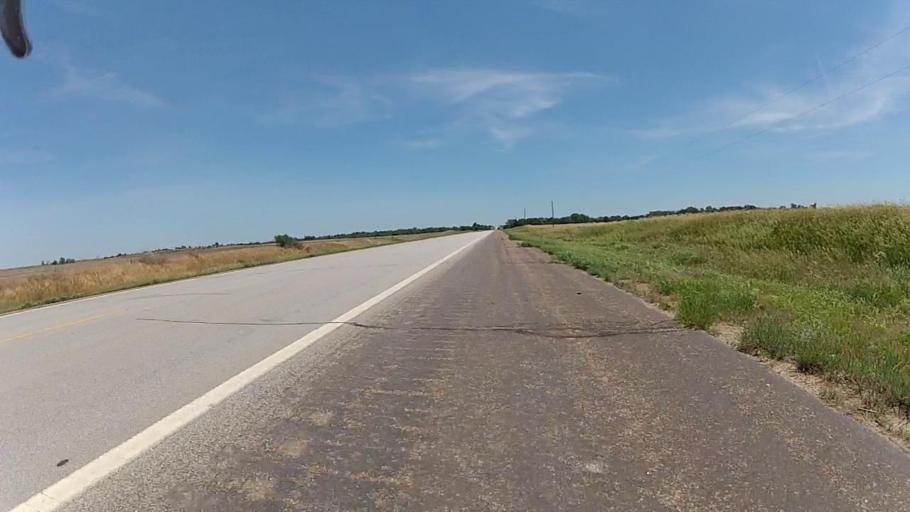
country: US
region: Kansas
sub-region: Barber County
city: Medicine Lodge
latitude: 37.2533
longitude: -98.3105
